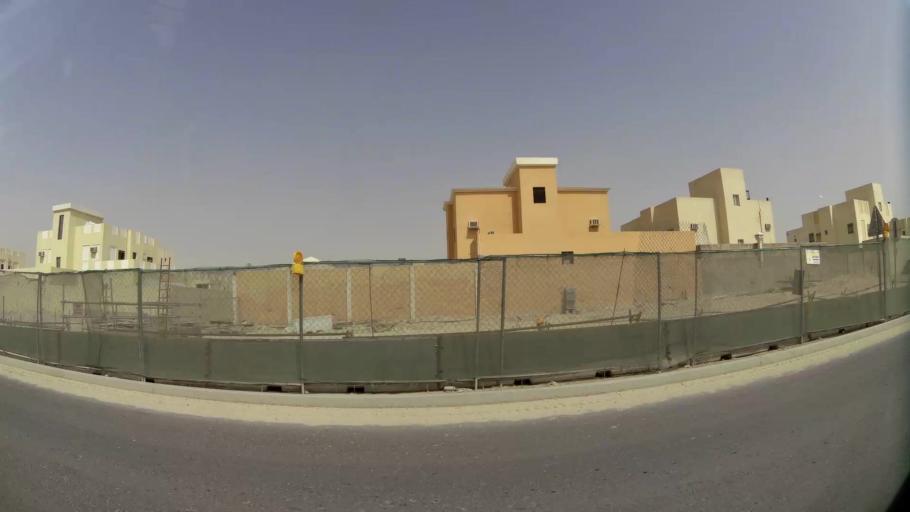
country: QA
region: Baladiyat ar Rayyan
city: Ar Rayyan
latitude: 25.2491
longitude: 51.3612
